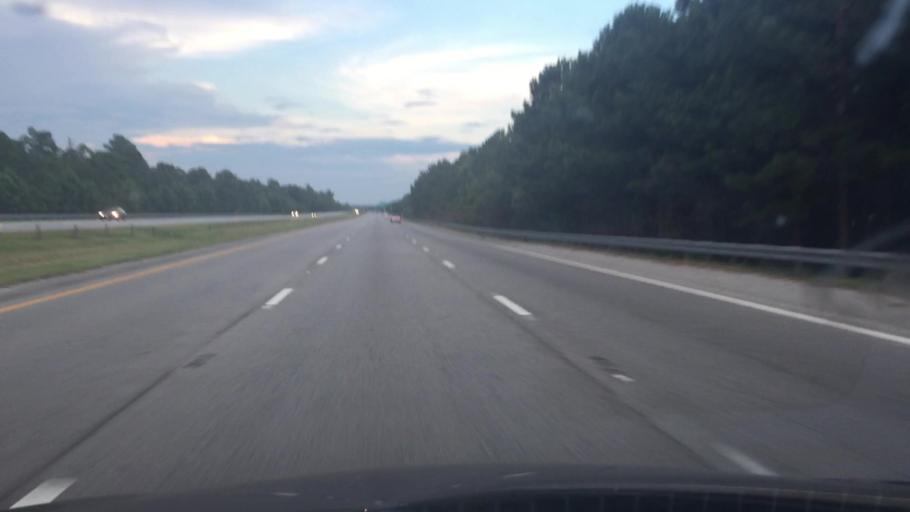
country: US
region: South Carolina
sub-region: Horry County
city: North Myrtle Beach
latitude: 33.8274
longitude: -78.7231
